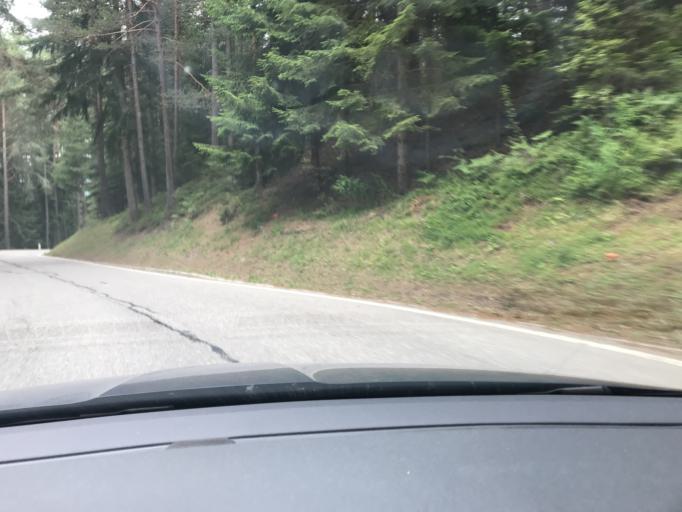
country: IT
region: Trentino-Alto Adige
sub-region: Bolzano
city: Bressanone
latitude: 46.6833
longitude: 11.6760
